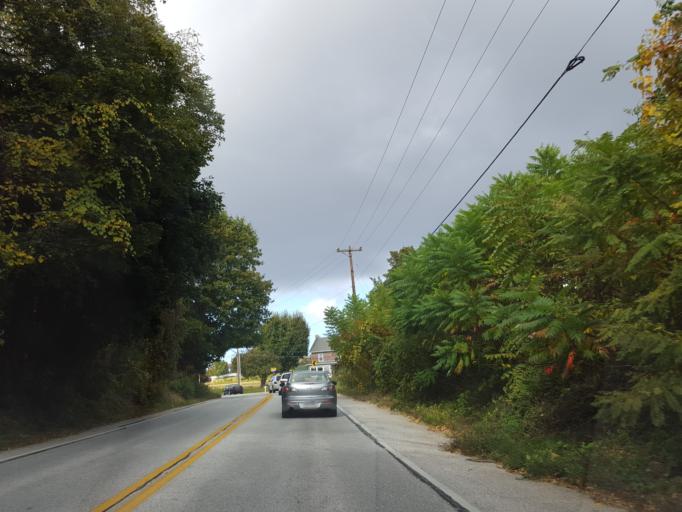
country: US
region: Pennsylvania
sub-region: York County
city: Spry
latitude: 39.9377
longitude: -76.6830
